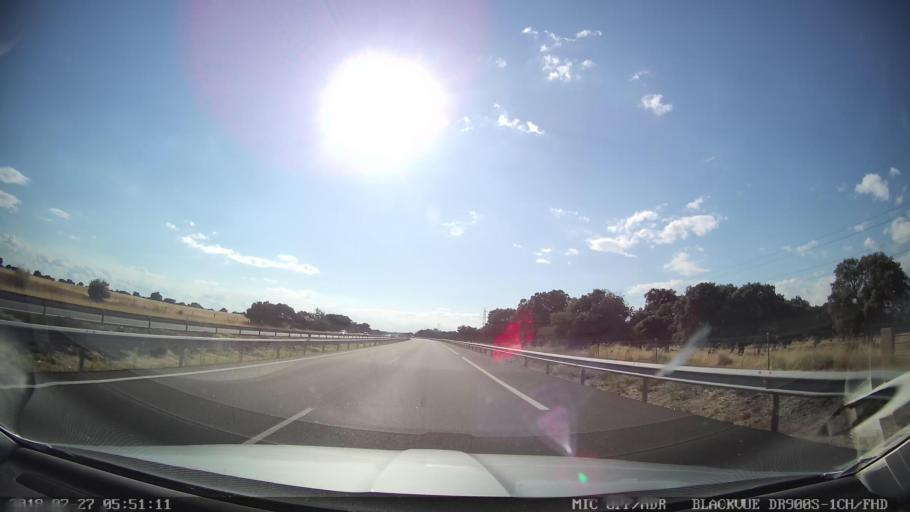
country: ES
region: Castille-La Mancha
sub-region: Province of Toledo
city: Alcanizo
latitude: 39.9231
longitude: -5.0913
